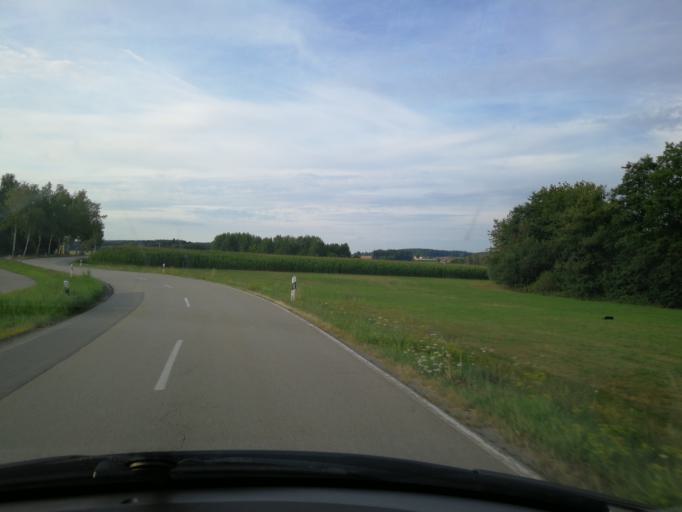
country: DE
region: Bavaria
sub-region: Lower Bavaria
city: Wiesenfelden
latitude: 49.0436
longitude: 12.5333
